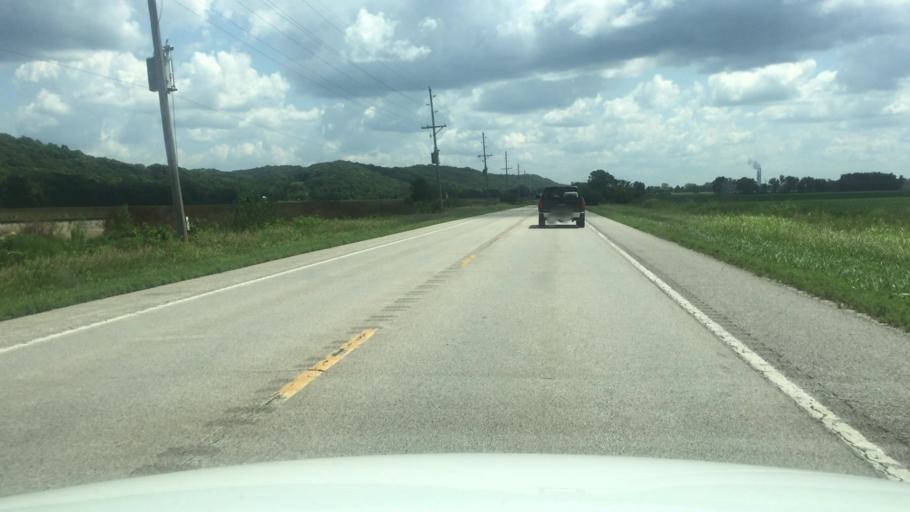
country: US
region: Kansas
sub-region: Atchison County
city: Atchison
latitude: 39.5185
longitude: -95.0237
